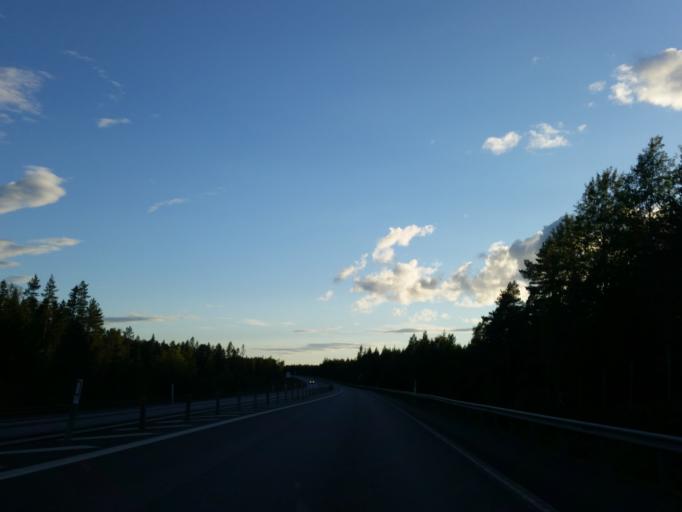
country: SE
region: Vaesterbotten
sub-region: Umea Kommun
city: Saevar
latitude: 63.9890
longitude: 20.7467
